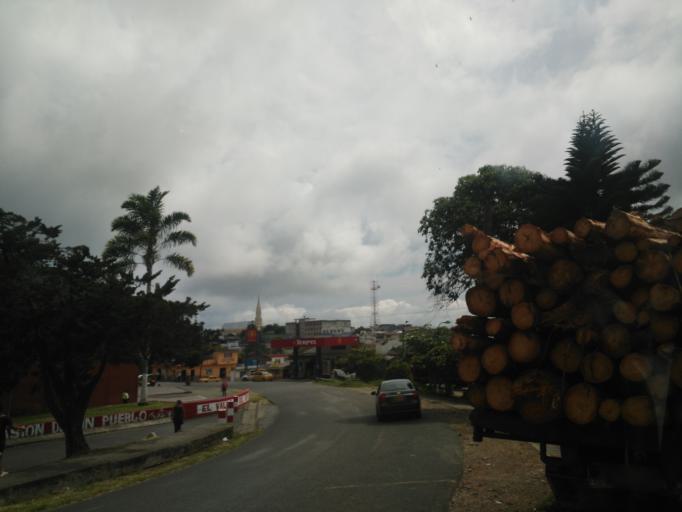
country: CO
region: Valle del Cauca
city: Sevilla
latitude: 4.2671
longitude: -75.9318
